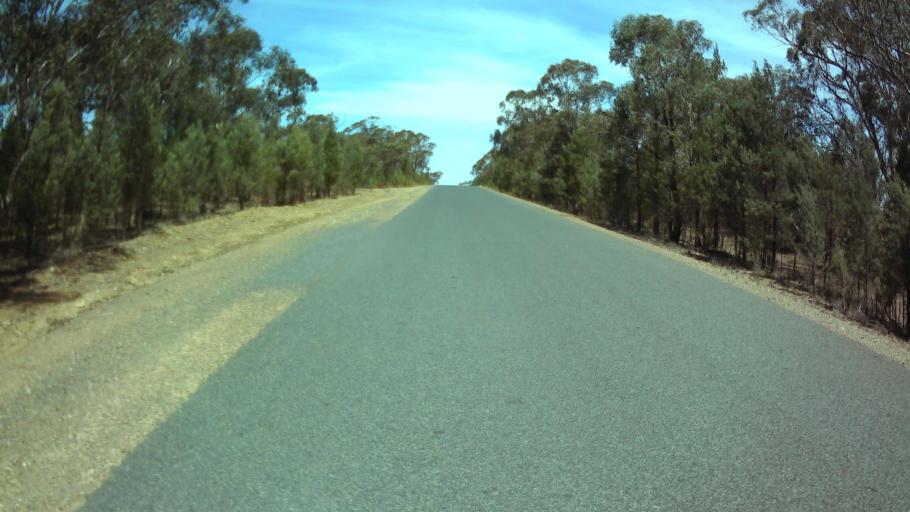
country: AU
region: New South Wales
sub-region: Weddin
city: Grenfell
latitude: -33.9004
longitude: 147.7551
